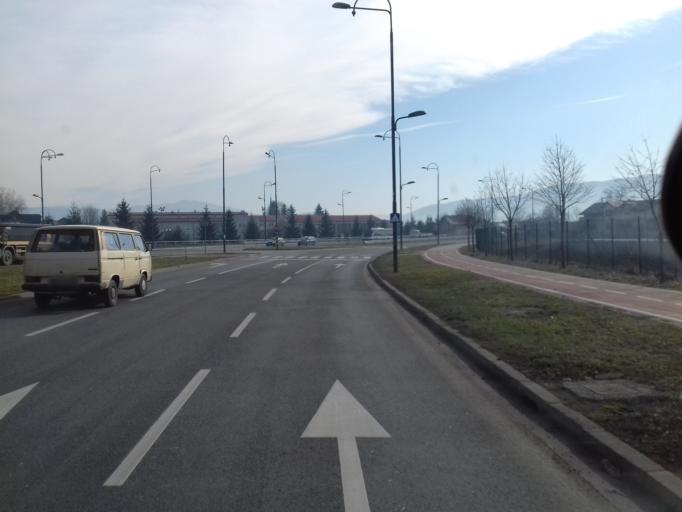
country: BA
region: Federation of Bosnia and Herzegovina
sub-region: Kanton Sarajevo
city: Sarajevo
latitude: 43.8244
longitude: 18.3188
